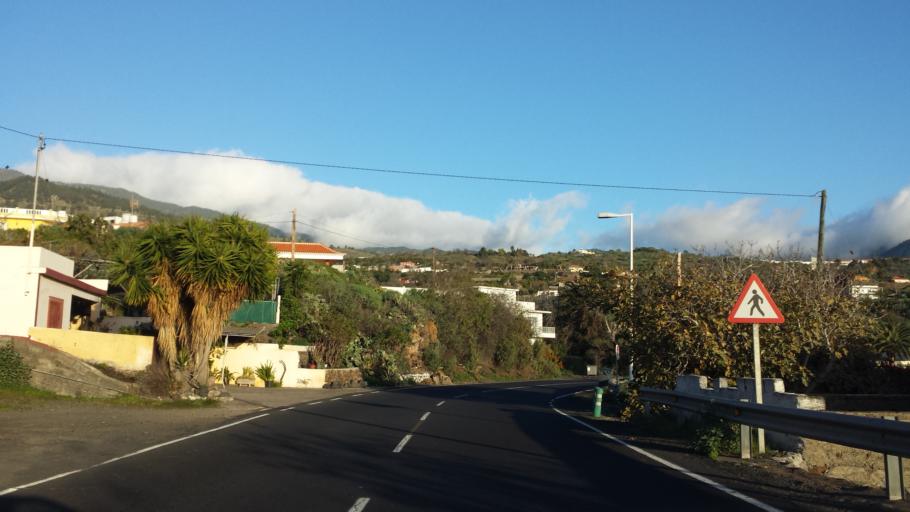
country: ES
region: Canary Islands
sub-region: Provincia de Santa Cruz de Tenerife
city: Los Llanos de Aridane
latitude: 28.6540
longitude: -17.9036
